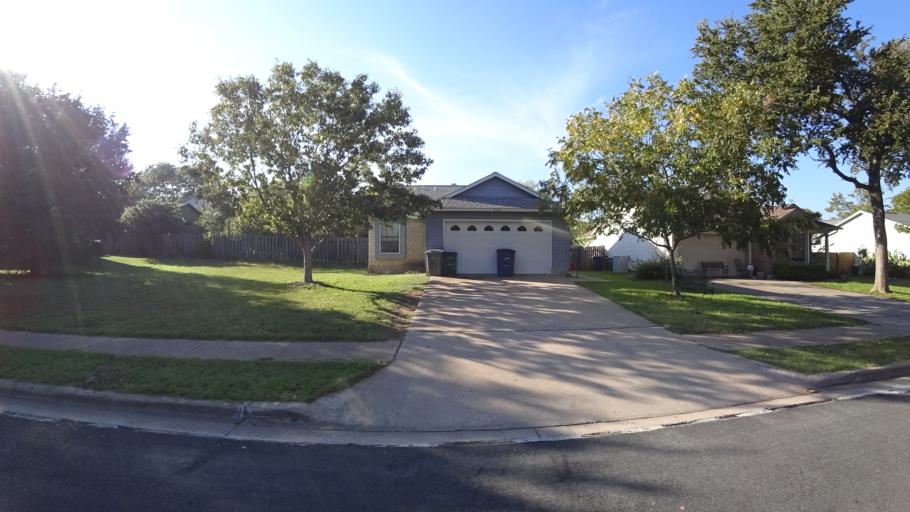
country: US
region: Texas
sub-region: Travis County
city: Shady Hollow
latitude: 30.2044
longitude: -97.8446
